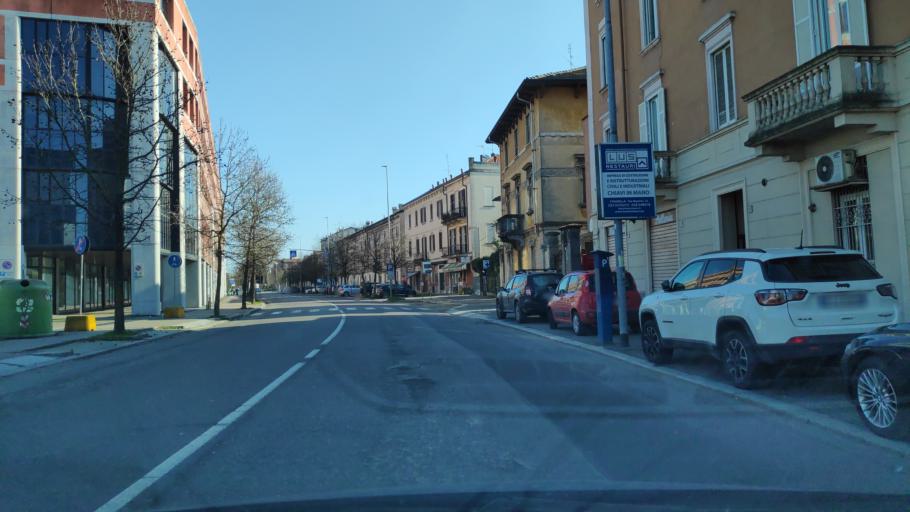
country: IT
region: Lombardy
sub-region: Provincia di Pavia
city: Pavia
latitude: 45.1939
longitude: 9.1544
